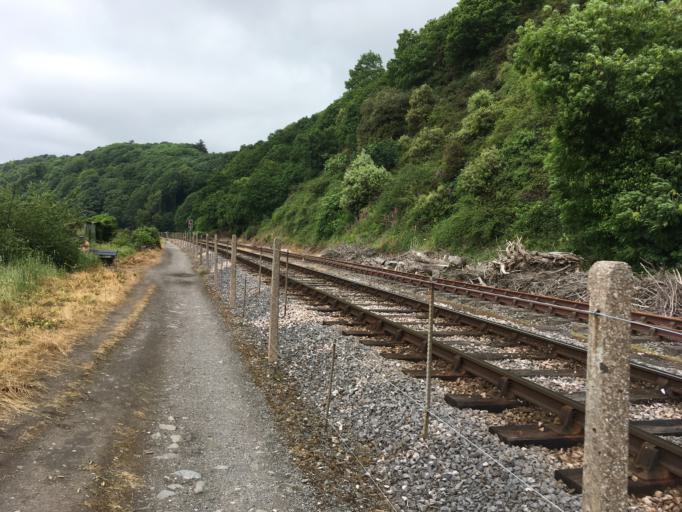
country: GB
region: England
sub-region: Devon
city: Dartmouth
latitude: 50.3541
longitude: -3.5700
